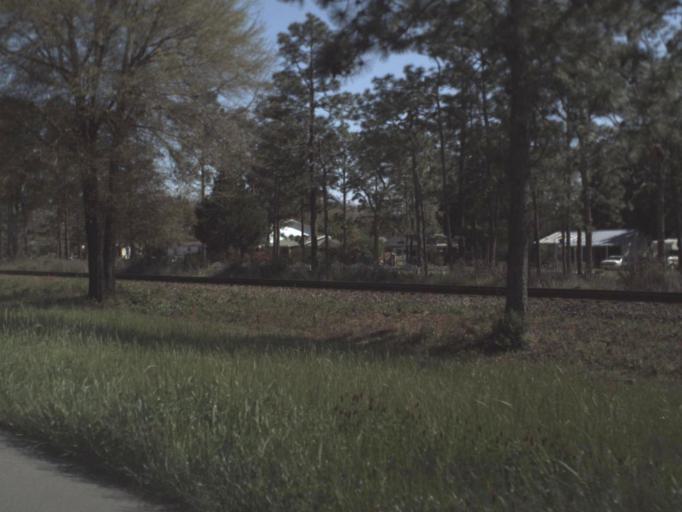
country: US
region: Florida
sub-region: Walton County
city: DeFuniak Springs
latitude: 30.7241
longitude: -86.0538
